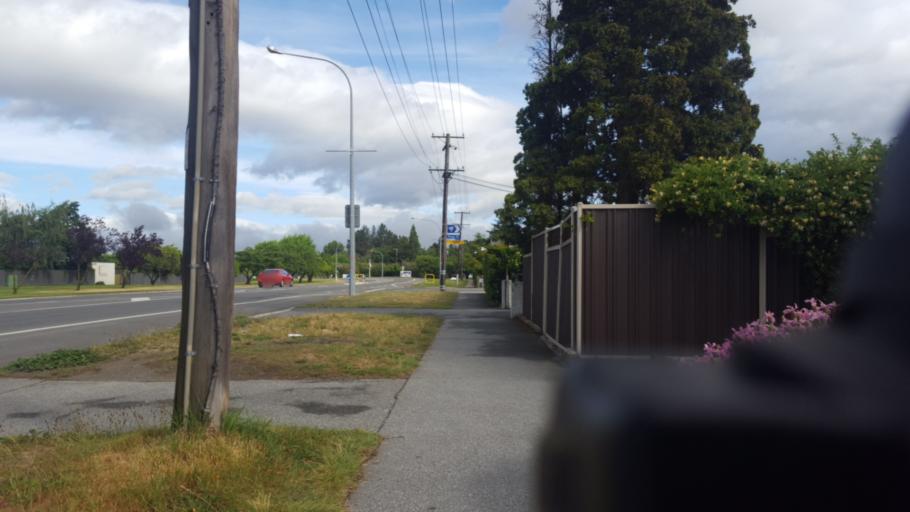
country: NZ
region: Otago
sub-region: Queenstown-Lakes District
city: Wanaka
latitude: -45.2463
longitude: 169.3829
